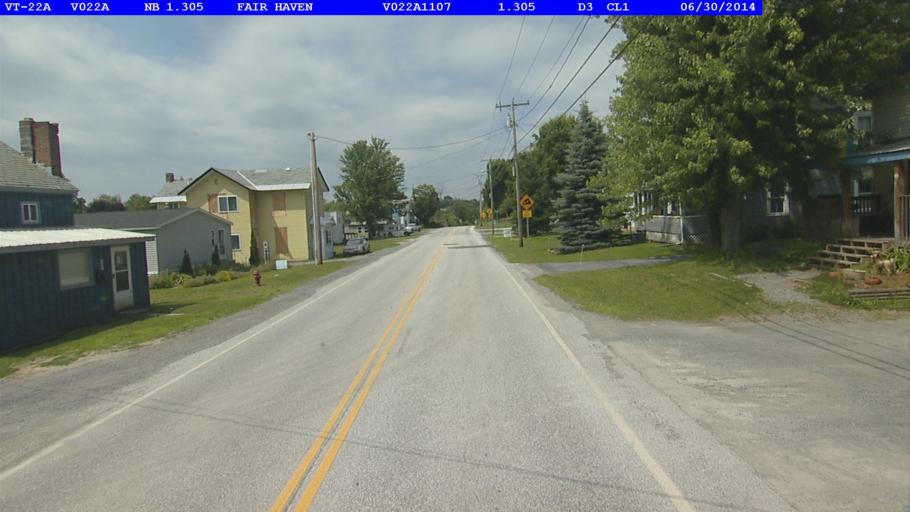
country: US
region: Vermont
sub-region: Rutland County
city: Fair Haven
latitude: 43.5869
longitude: -73.2652
